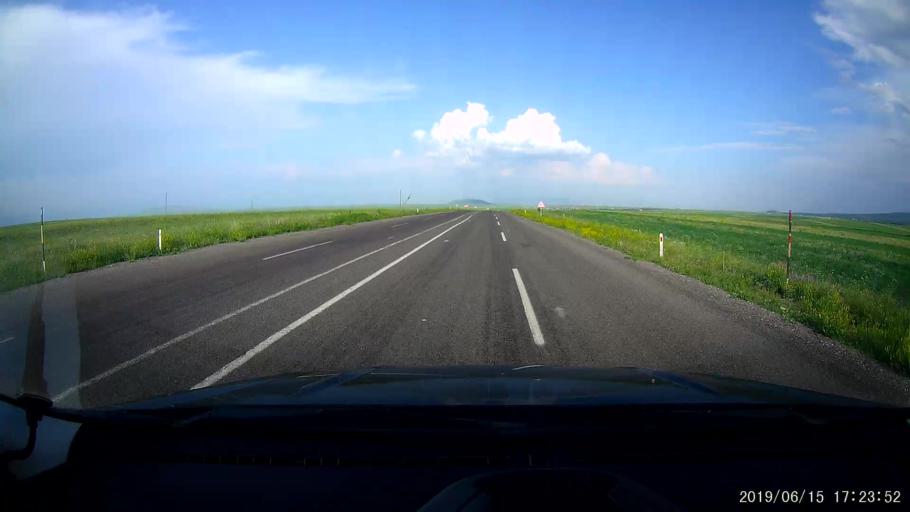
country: TR
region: Kars
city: Basgedikler
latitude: 40.6163
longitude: 43.3720
